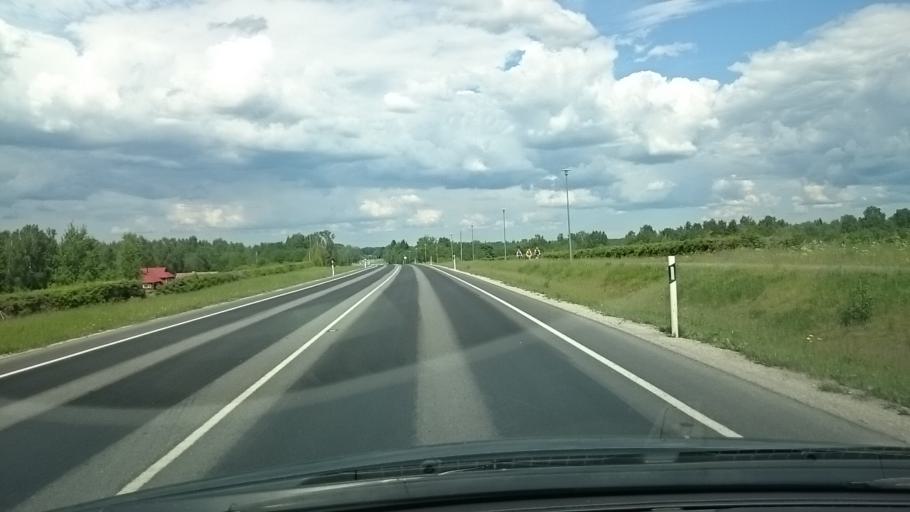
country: EE
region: Jaervamaa
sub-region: Tueri vald
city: Tueri
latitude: 58.8394
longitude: 25.4744
